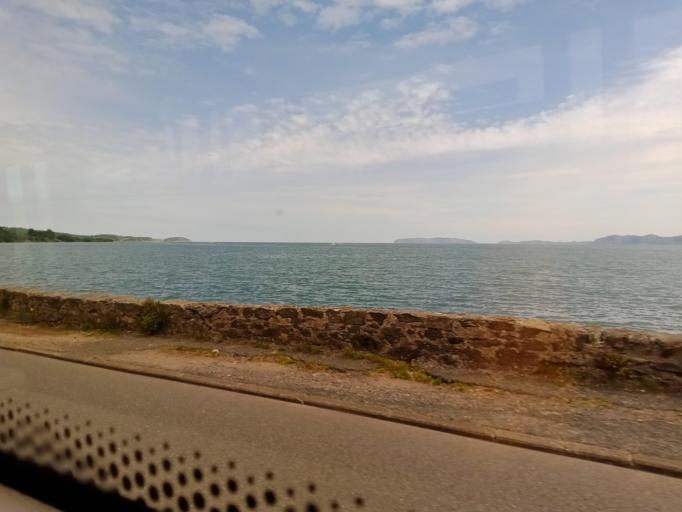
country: GB
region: Wales
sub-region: Anglesey
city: Beaumaris
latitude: 53.2703
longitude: -4.0862
